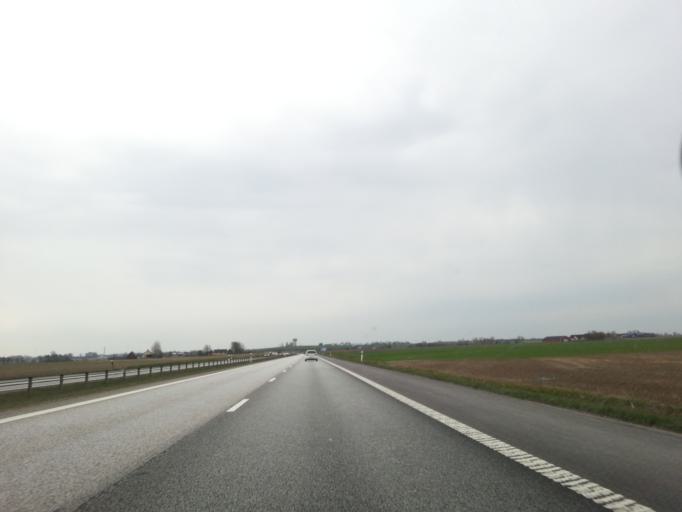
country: SE
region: Skane
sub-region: Angelholms Kommun
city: AEngelholm
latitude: 56.2779
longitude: 12.8967
